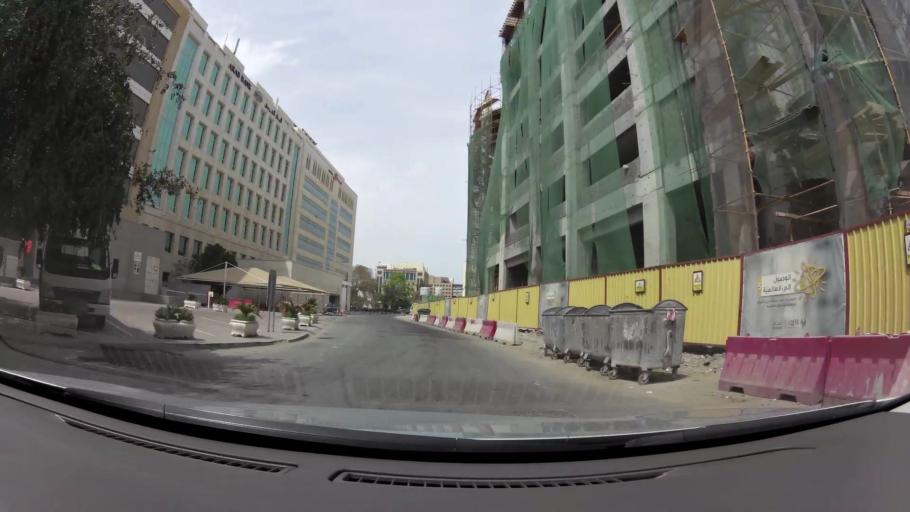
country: QA
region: Baladiyat ad Dawhah
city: Doha
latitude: 25.2816
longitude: 51.5360
